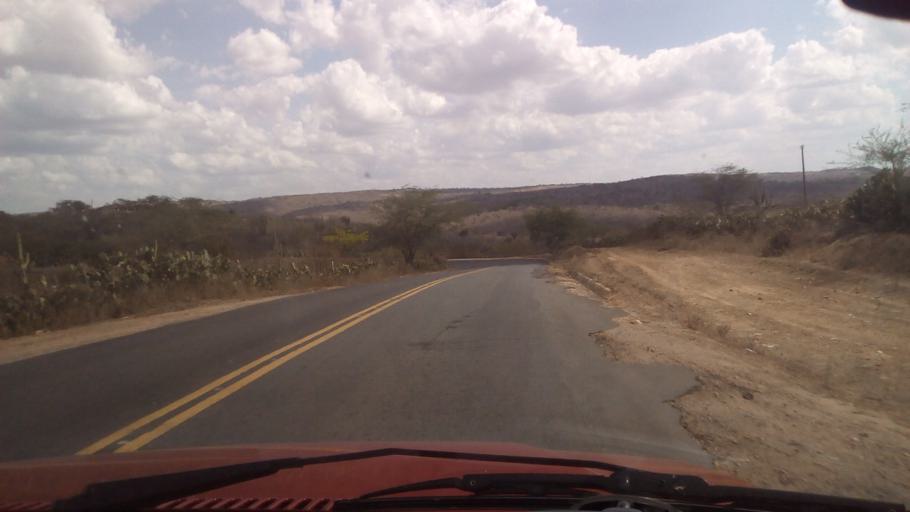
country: BR
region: Paraiba
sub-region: Bananeiras
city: Bananeiras
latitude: -6.7133
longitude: -35.7212
